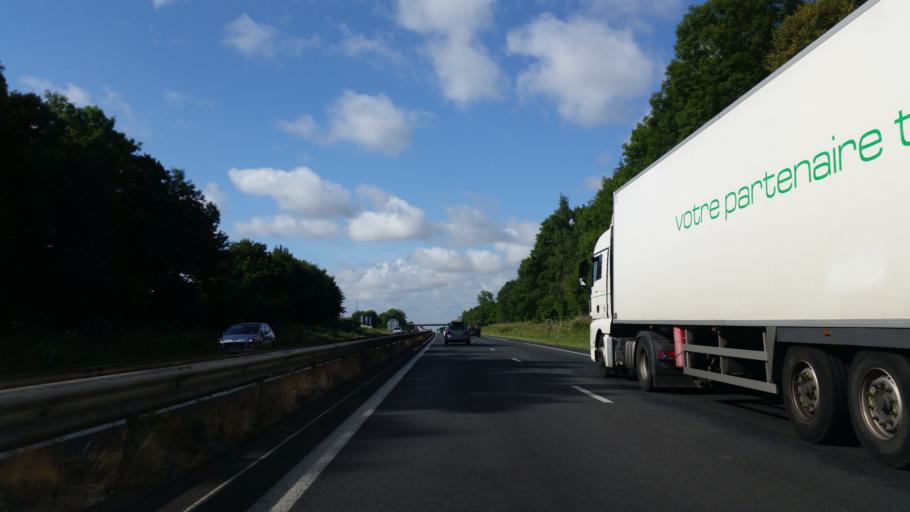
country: FR
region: Lower Normandy
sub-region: Departement du Calvados
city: Troarn
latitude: 49.1930
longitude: -0.1870
